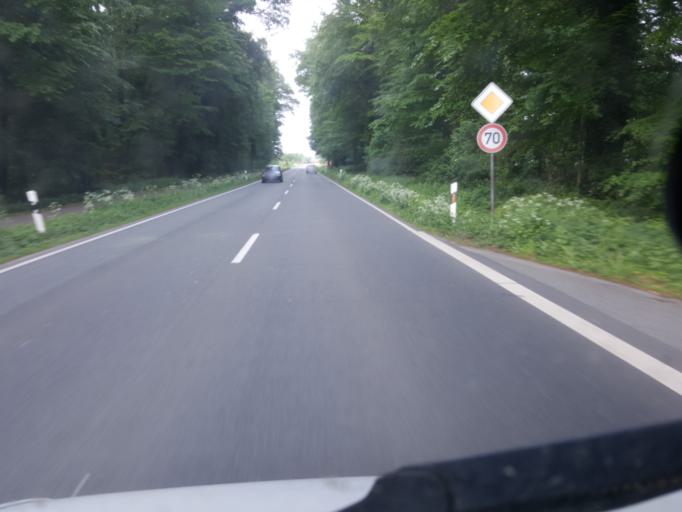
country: DE
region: Lower Saxony
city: Binnen
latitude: 52.6221
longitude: 9.1225
